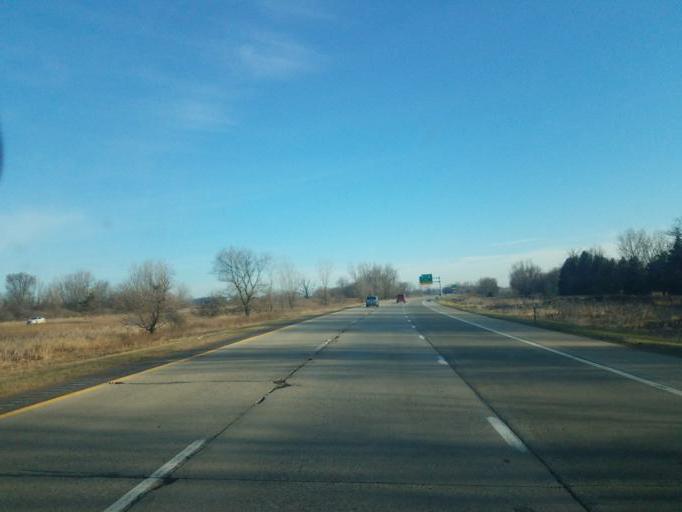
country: US
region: Michigan
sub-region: Ingham County
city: East Lansing
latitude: 42.7904
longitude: -84.5135
